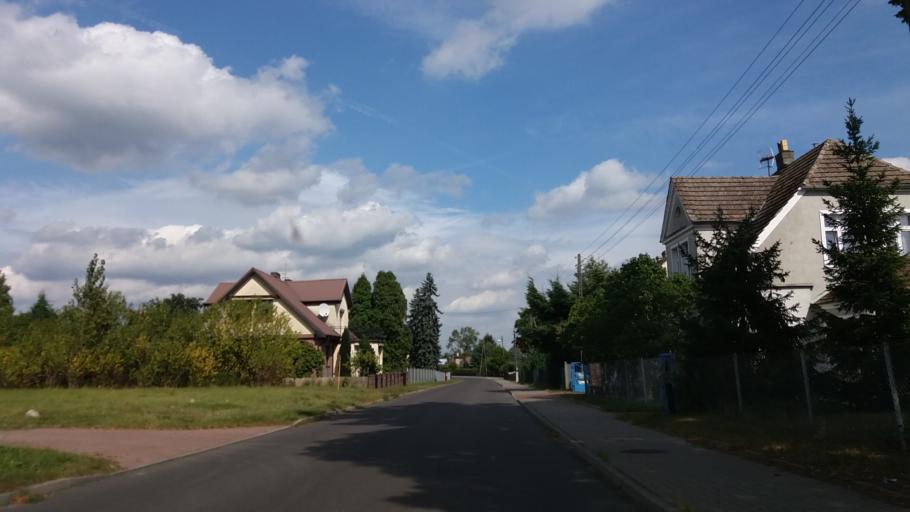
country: PL
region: West Pomeranian Voivodeship
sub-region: Powiat stargardzki
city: Kobylanka
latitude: 53.3506
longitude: 14.8685
